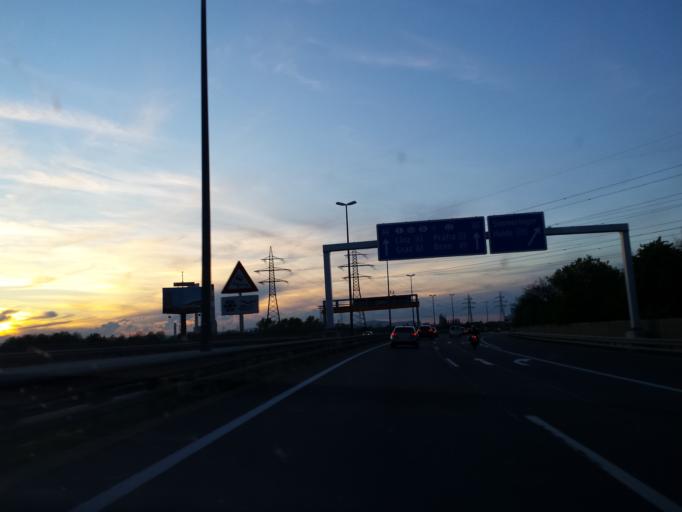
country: AT
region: Lower Austria
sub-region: Politischer Bezirk Wien-Umgebung
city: Schwechat
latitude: 48.1693
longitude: 16.4572
